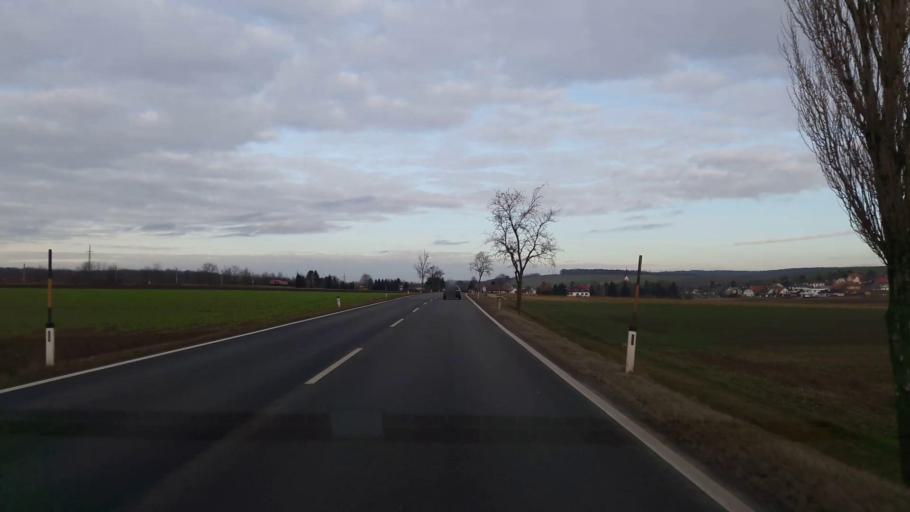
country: AT
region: Lower Austria
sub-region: Politischer Bezirk Mistelbach
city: Mistelbach
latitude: 48.5985
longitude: 16.5437
